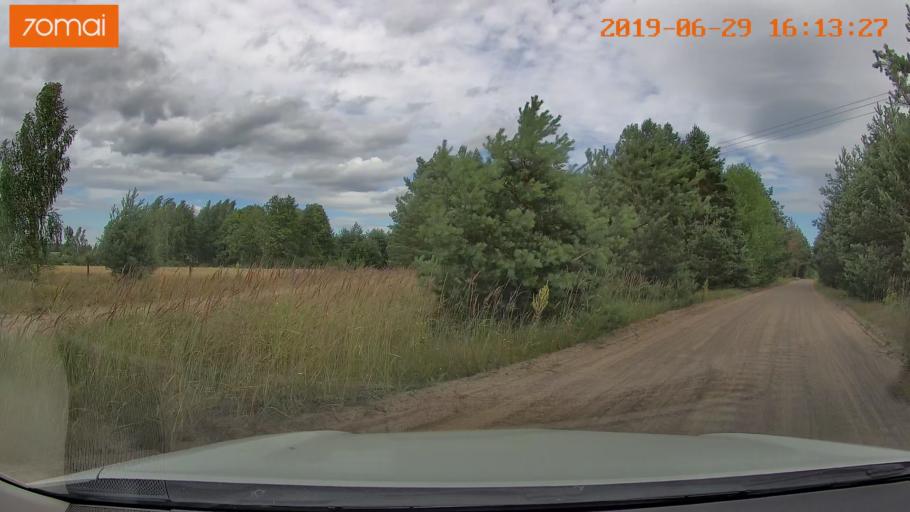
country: BY
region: Brest
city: Luninyets
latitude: 52.1988
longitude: 27.0206
